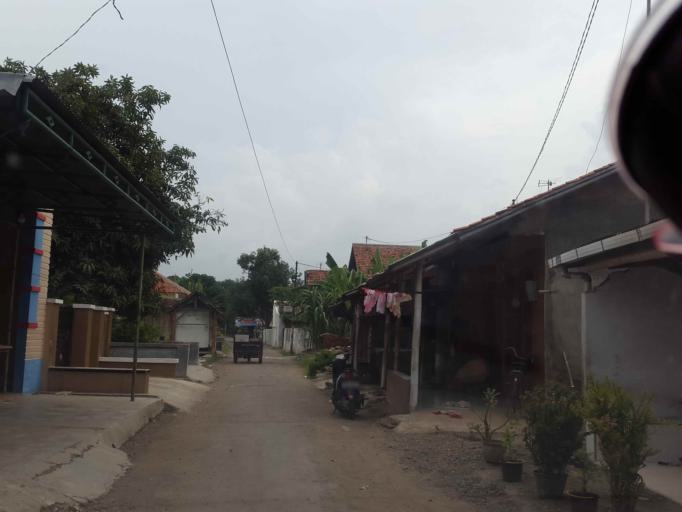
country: ID
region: Central Java
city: Dukuhturi
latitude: -6.8781
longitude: 109.0992
